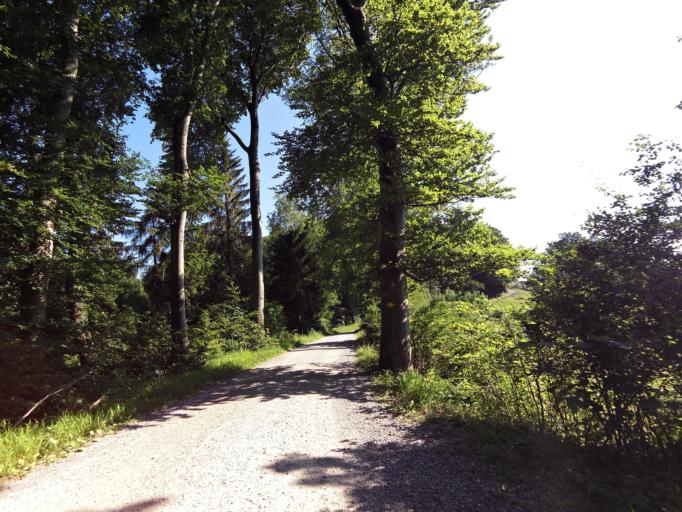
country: CH
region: Zurich
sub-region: Bezirk Zuerich
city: Zuerich (Kreis 3)
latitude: 47.3445
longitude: 8.4982
